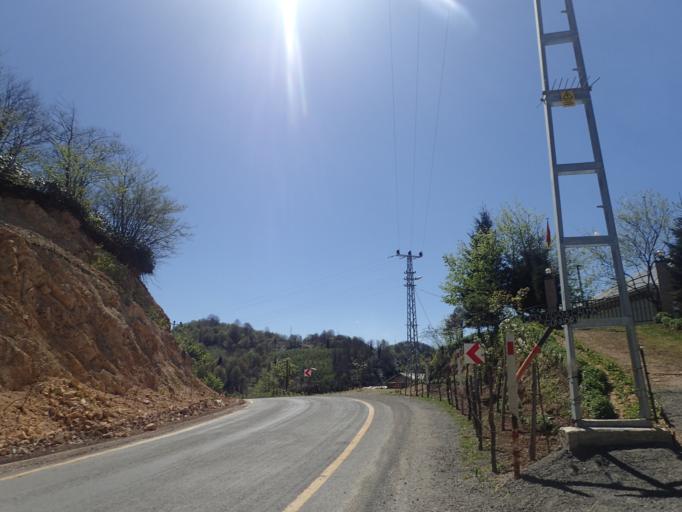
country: TR
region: Ordu
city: Kabaduz
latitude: 40.7986
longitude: 37.9128
